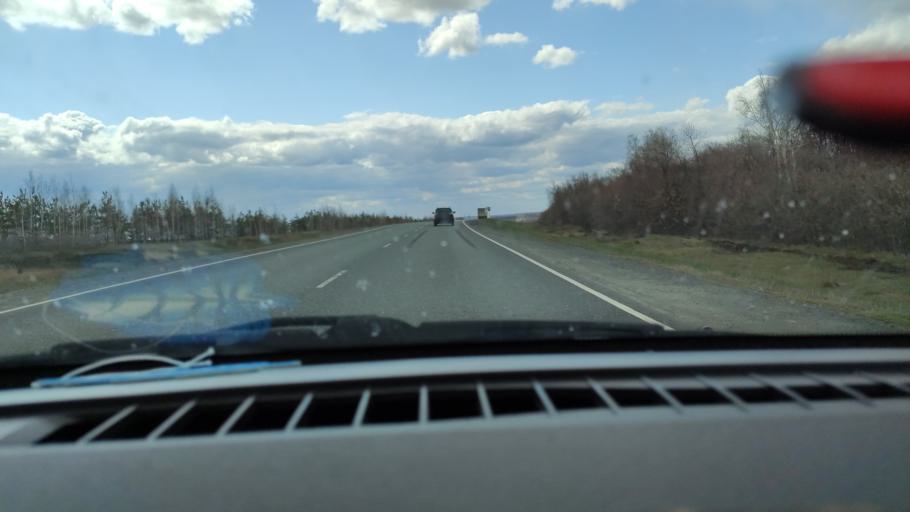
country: RU
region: Saratov
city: Balakovo
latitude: 52.1587
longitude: 47.8195
